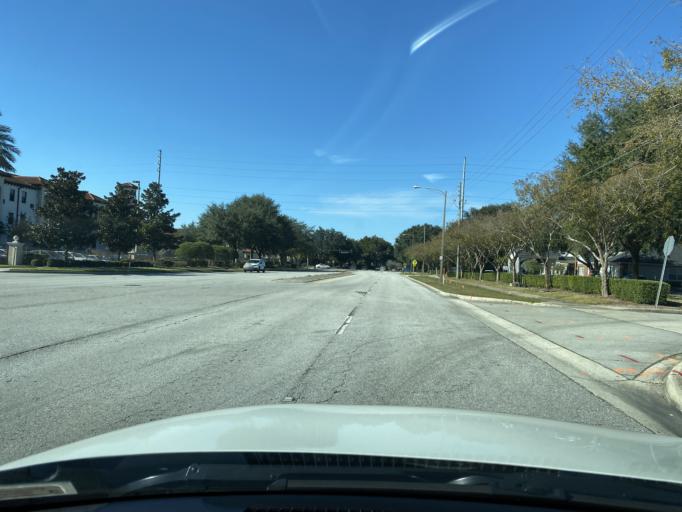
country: US
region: Florida
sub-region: Orange County
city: Conway
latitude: 28.5147
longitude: -81.3127
